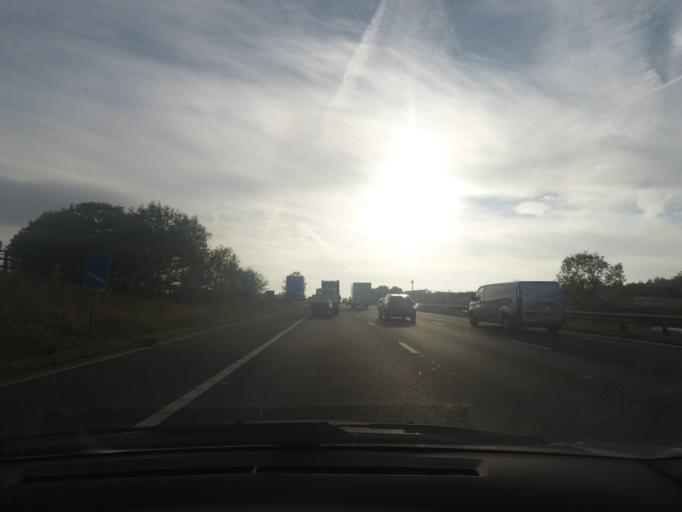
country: GB
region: England
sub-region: Barnsley
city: Dodworth
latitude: 53.5550
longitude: -1.5264
